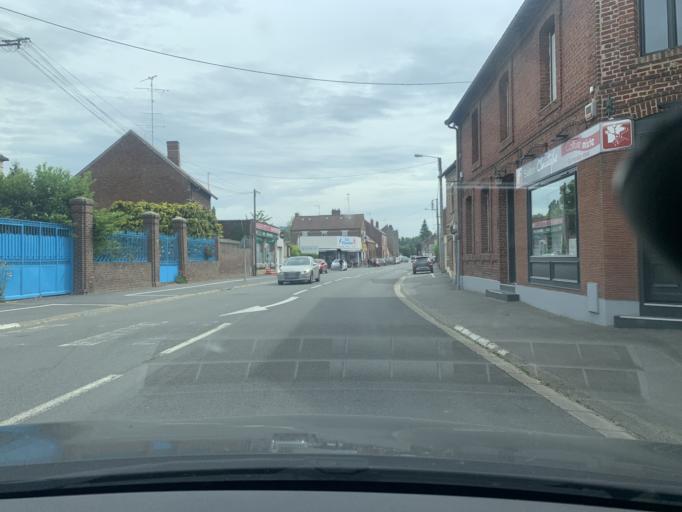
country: FR
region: Nord-Pas-de-Calais
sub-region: Departement du Nord
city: Marcoing
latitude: 50.1219
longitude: 3.1738
